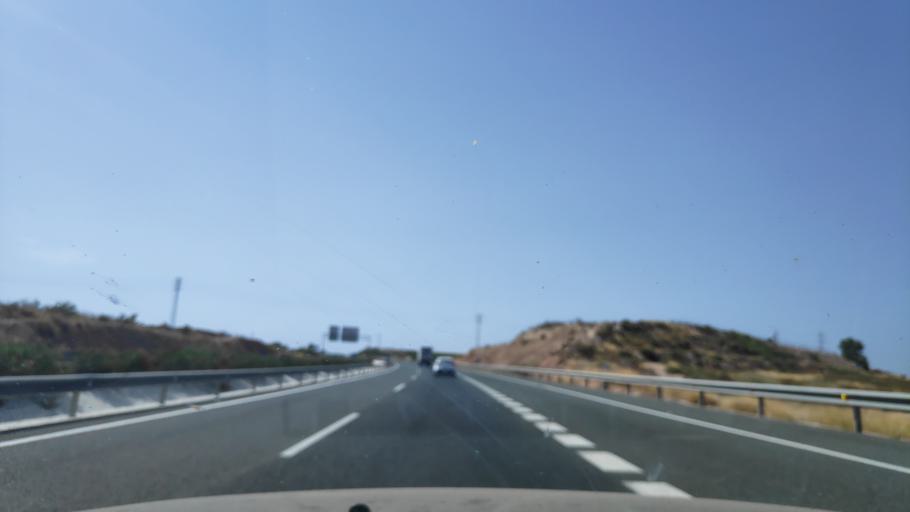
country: ES
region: Murcia
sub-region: Murcia
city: Blanca
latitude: 38.1955
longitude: -1.3338
